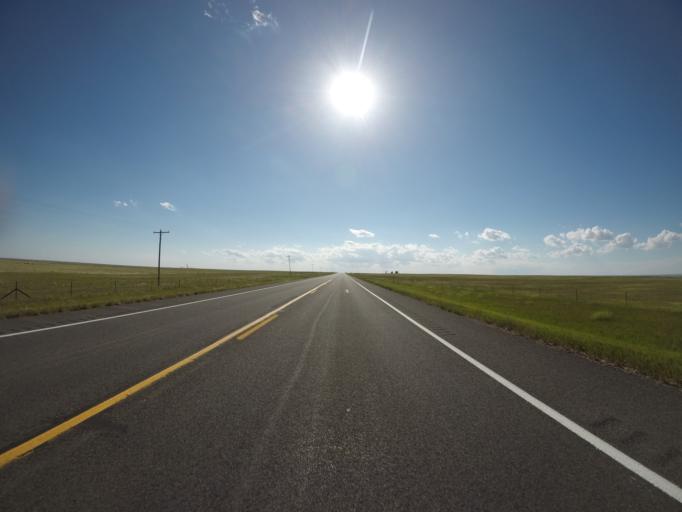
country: US
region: Colorado
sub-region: Morgan County
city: Brush
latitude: 40.6102
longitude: -103.6497
